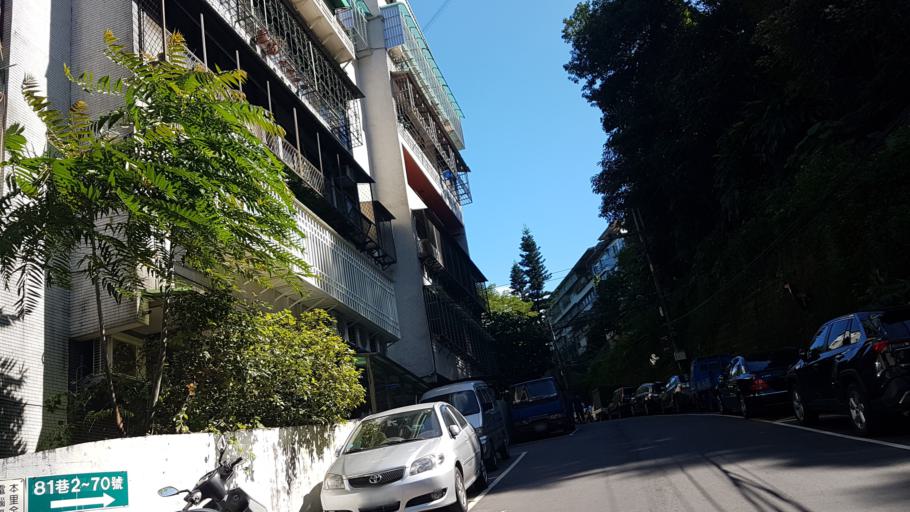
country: TW
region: Taipei
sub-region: Taipei
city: Banqiao
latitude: 24.9490
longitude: 121.5301
